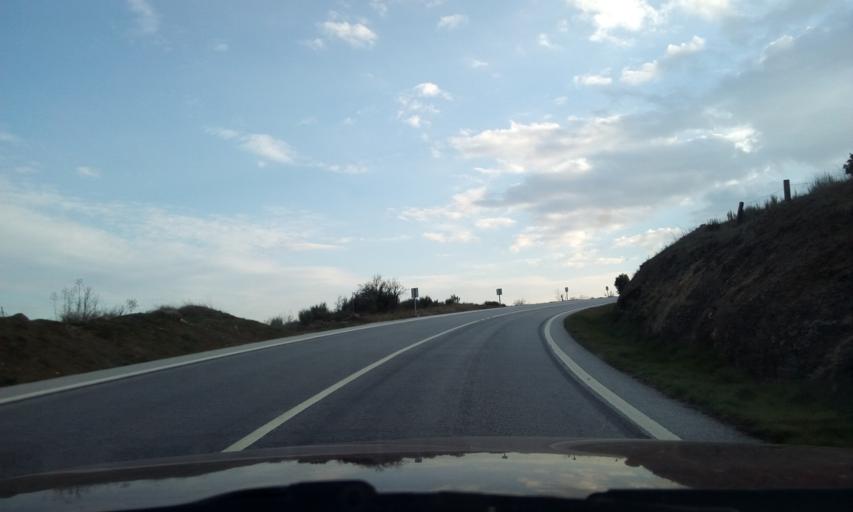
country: ES
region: Castille and Leon
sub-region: Provincia de Salamanca
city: Aldea del Obispo
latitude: 40.6953
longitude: -6.9349
